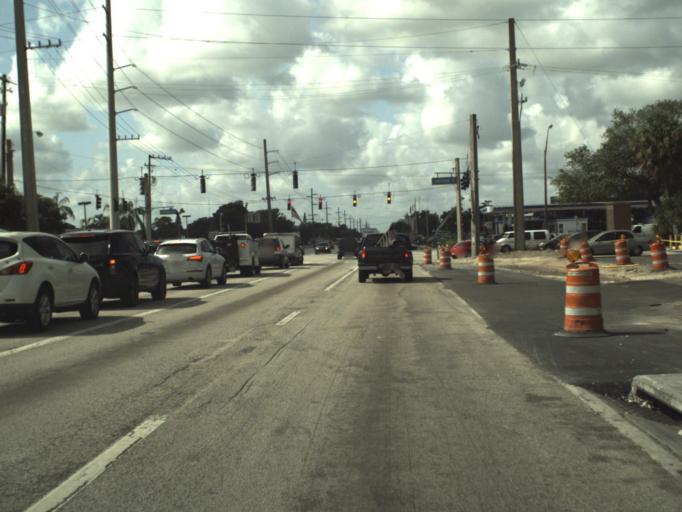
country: US
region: Florida
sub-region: Broward County
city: Pembroke Pines
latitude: 26.0329
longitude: -80.2085
